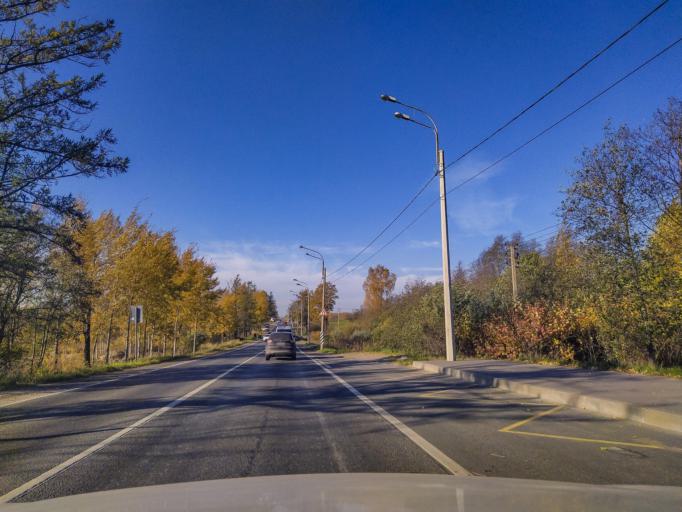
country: RU
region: St.-Petersburg
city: Aleksandrovskaya
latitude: 59.7078
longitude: 30.3306
